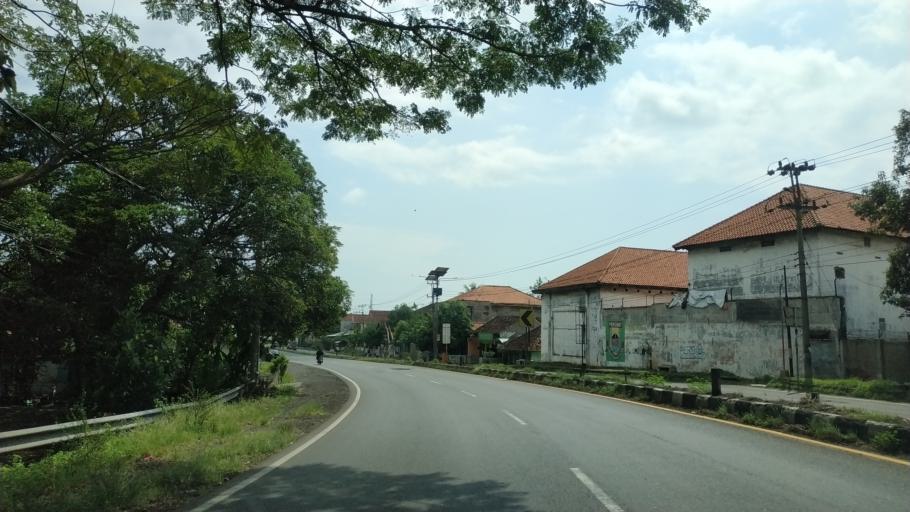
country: ID
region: Central Java
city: Pekalongan
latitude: -6.9518
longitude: 109.8083
